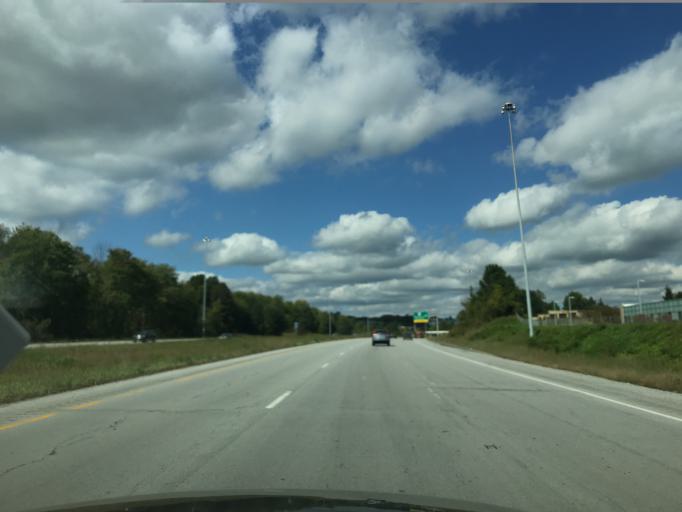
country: US
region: Ohio
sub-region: Summit County
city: Twinsburg
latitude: 41.3079
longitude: -81.4456
